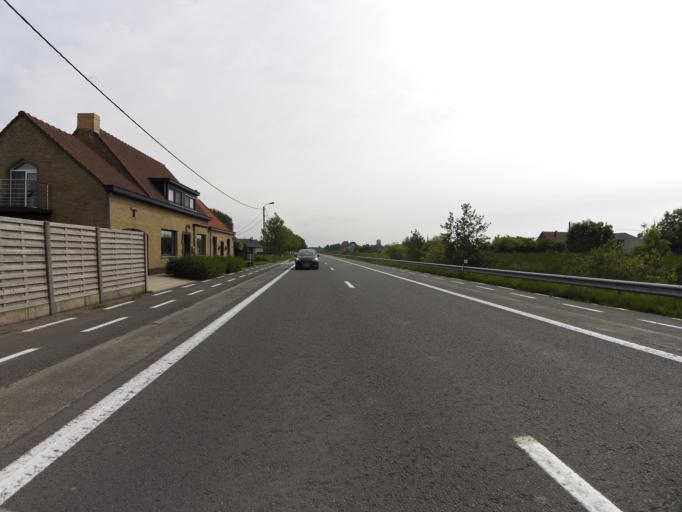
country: BE
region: Flanders
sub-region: Provincie West-Vlaanderen
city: Veurne
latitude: 51.0808
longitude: 2.6708
